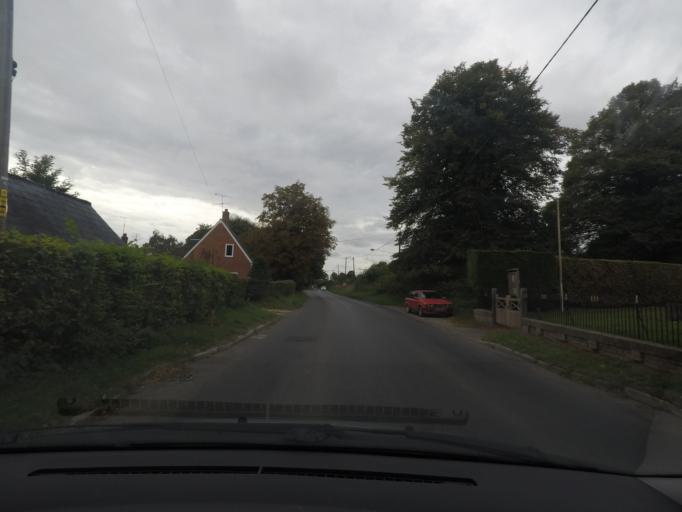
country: GB
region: England
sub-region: Wiltshire
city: Huish
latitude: 51.3653
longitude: -1.7751
